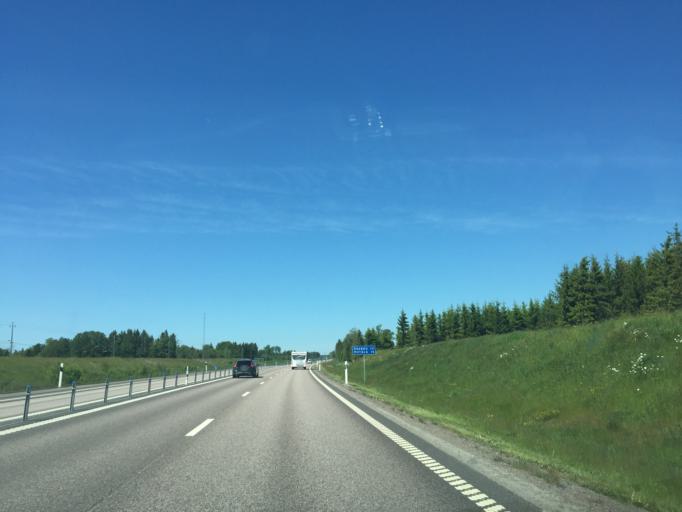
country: SE
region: OEstergoetland
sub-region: Motala Kommun
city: Stenstorp
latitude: 58.4094
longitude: 15.0808
